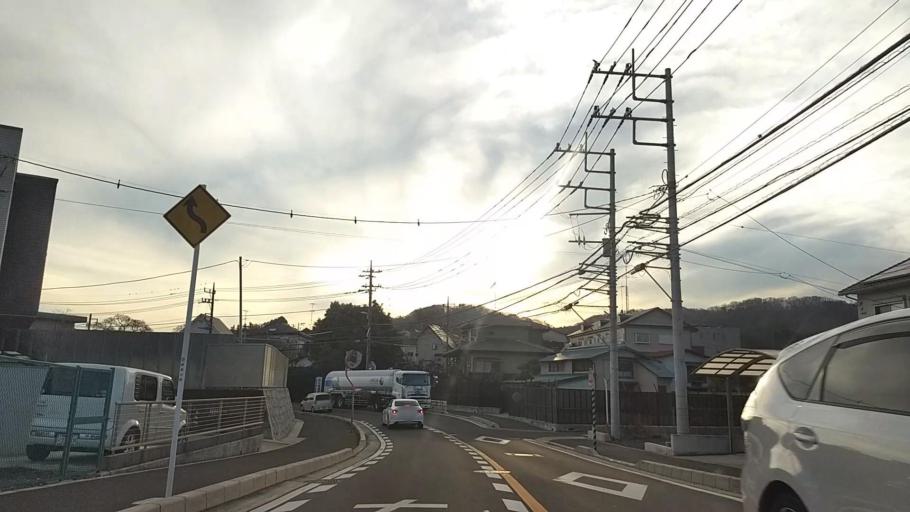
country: JP
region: Kanagawa
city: Atsugi
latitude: 35.4496
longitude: 139.3284
